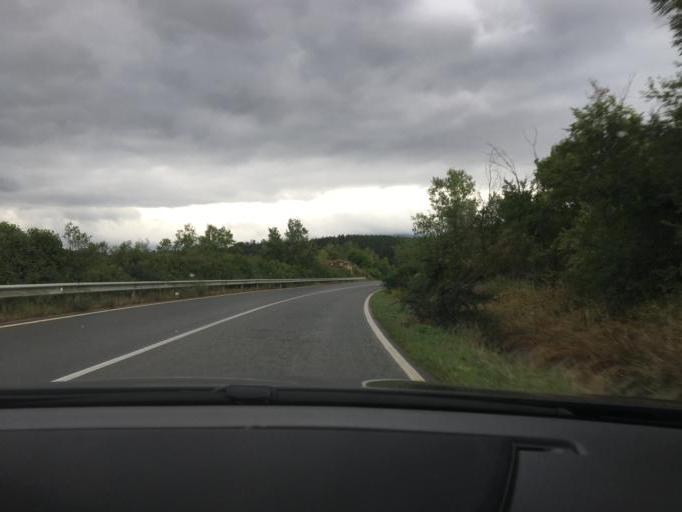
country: BG
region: Kyustendil
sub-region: Obshtina Boboshevo
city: Boboshevo
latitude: 42.2523
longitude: 22.8867
